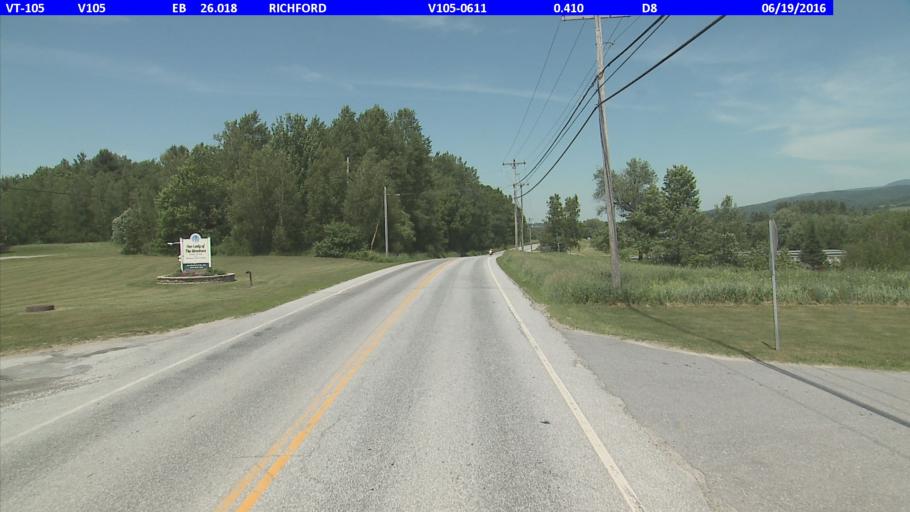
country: US
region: Vermont
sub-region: Franklin County
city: Richford
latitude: 44.9774
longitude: -72.6875
